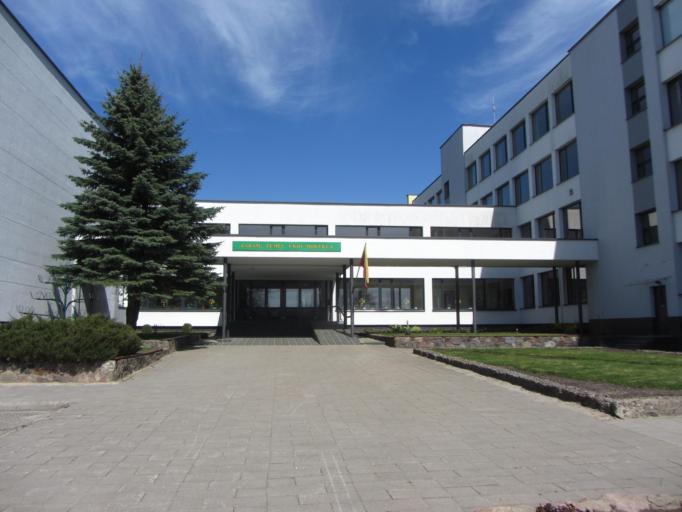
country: LT
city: Zarasai
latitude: 55.7425
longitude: 26.2713
